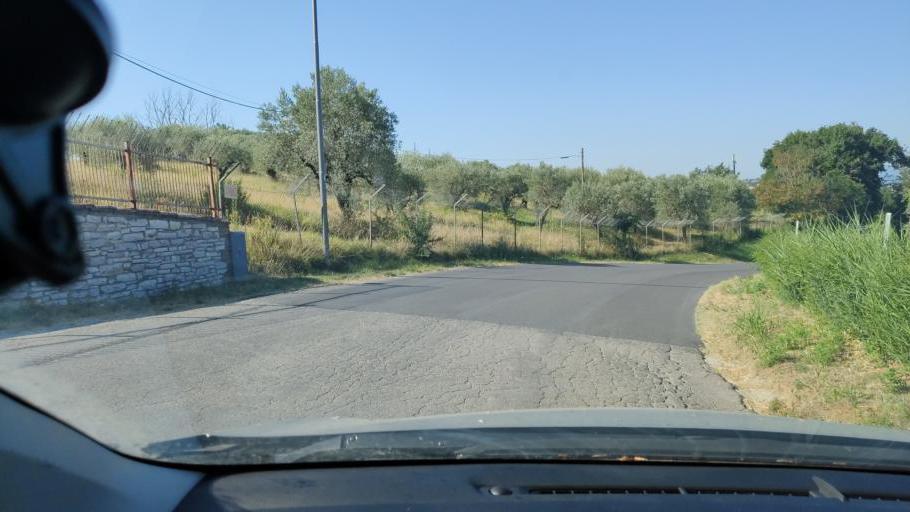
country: IT
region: Umbria
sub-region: Provincia di Terni
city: Fornole
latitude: 42.5371
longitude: 12.4542
